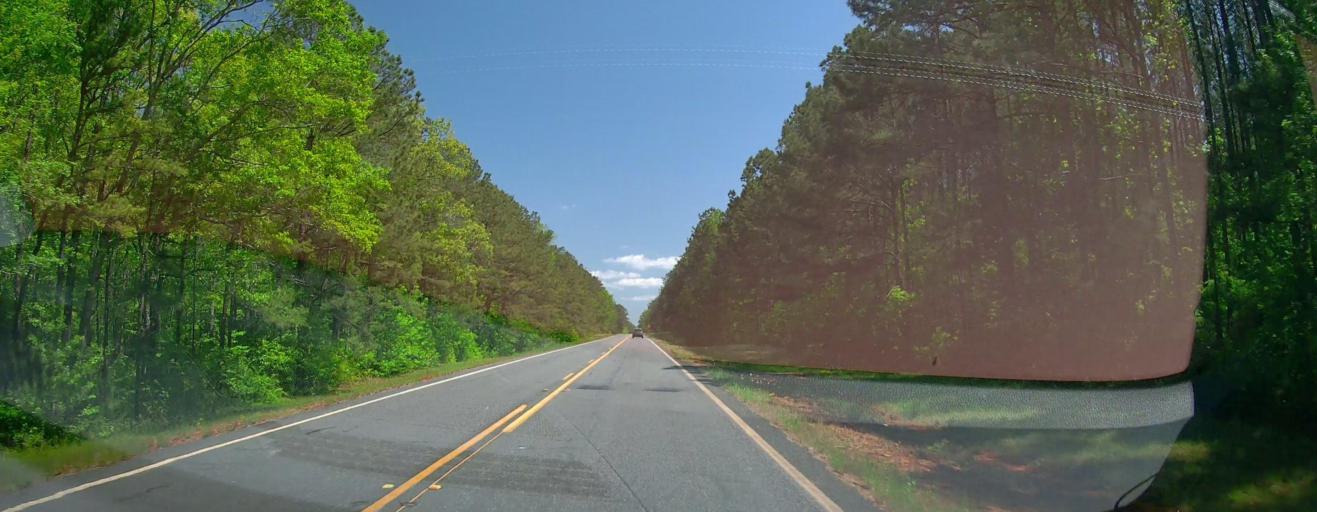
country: US
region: Georgia
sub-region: Putnam County
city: Eatonton
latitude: 33.2308
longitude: -83.5181
